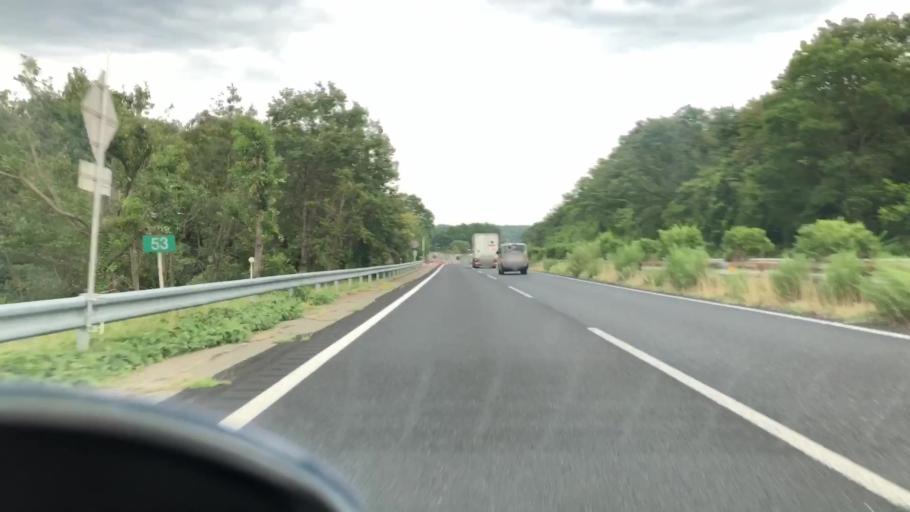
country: JP
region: Hyogo
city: Yashiro
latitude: 34.9148
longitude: 135.0304
